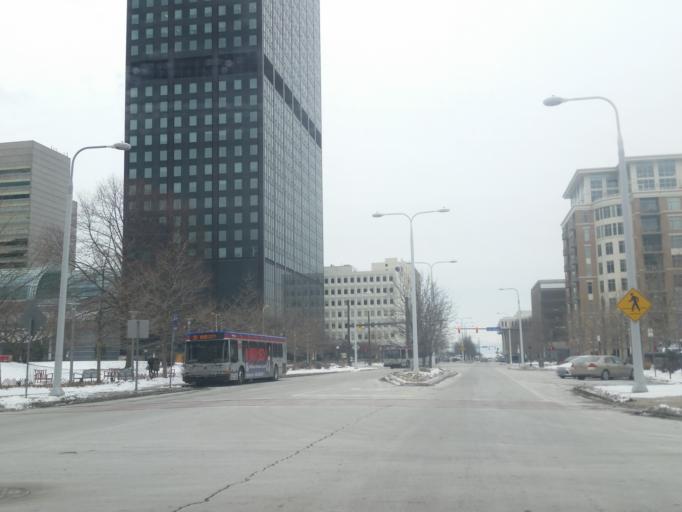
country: US
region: Ohio
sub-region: Cuyahoga County
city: Cleveland
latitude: 41.5043
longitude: -81.6869
